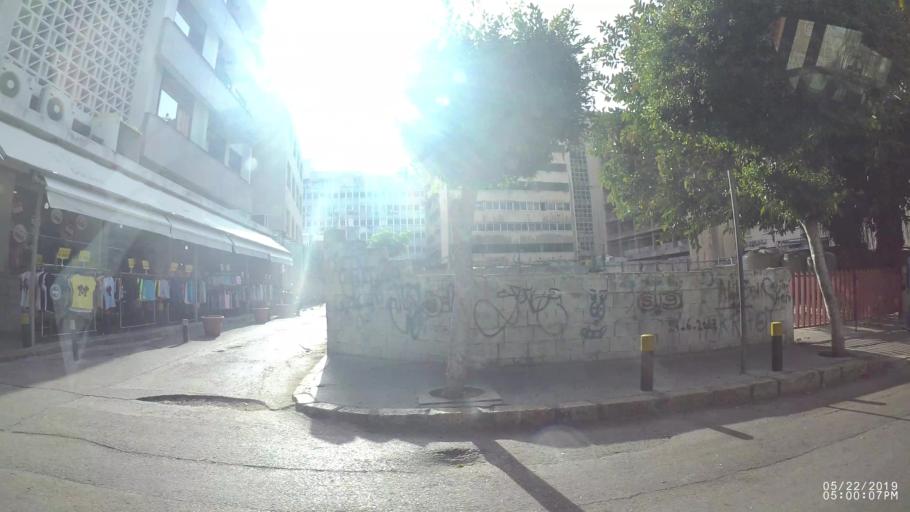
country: LB
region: Beyrouth
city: Ra's Bayrut
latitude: 33.8948
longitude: 35.4848
